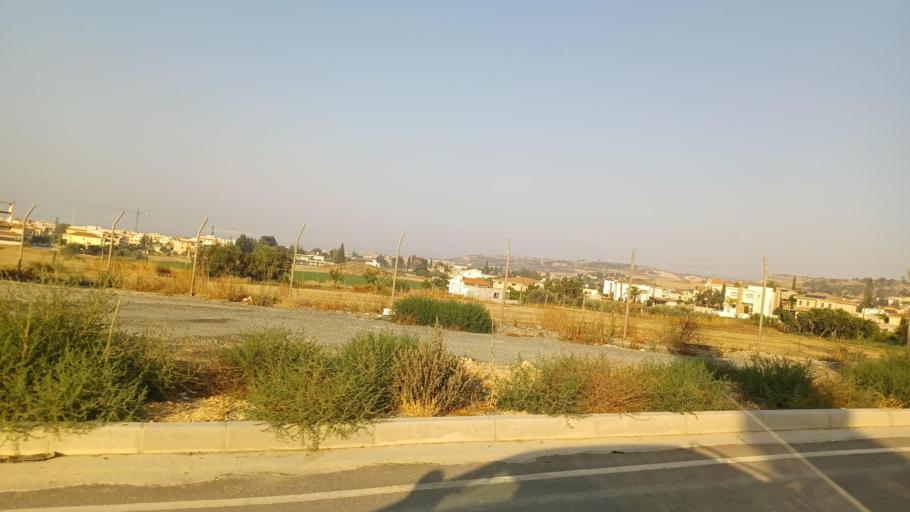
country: CY
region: Larnaka
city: Pyla
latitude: 35.0130
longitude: 33.6974
